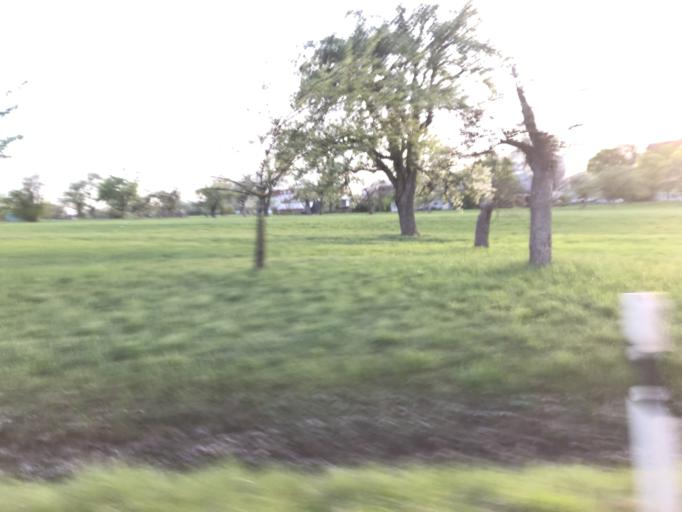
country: DE
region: Baden-Wuerttemberg
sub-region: Regierungsbezirk Stuttgart
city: Filderstadt
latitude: 48.6723
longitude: 9.2204
